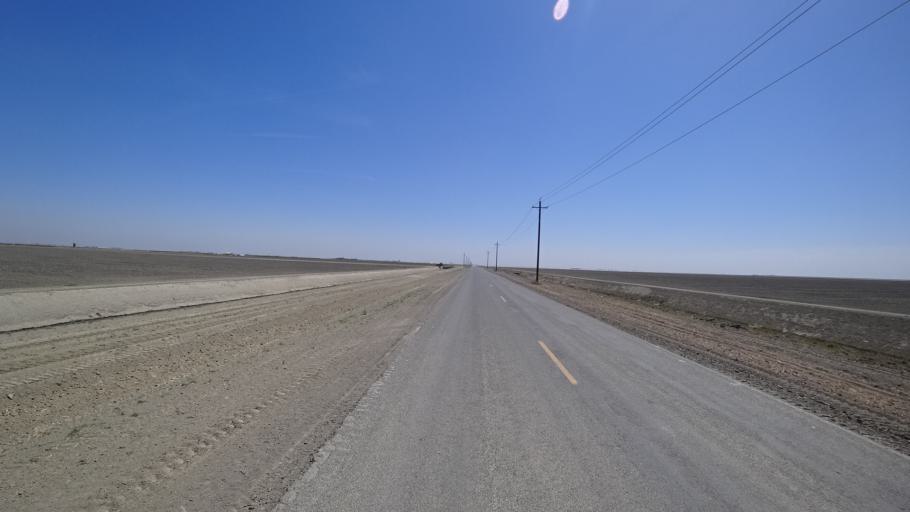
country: US
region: California
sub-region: Kings County
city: Corcoran
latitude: 36.0215
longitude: -119.6104
